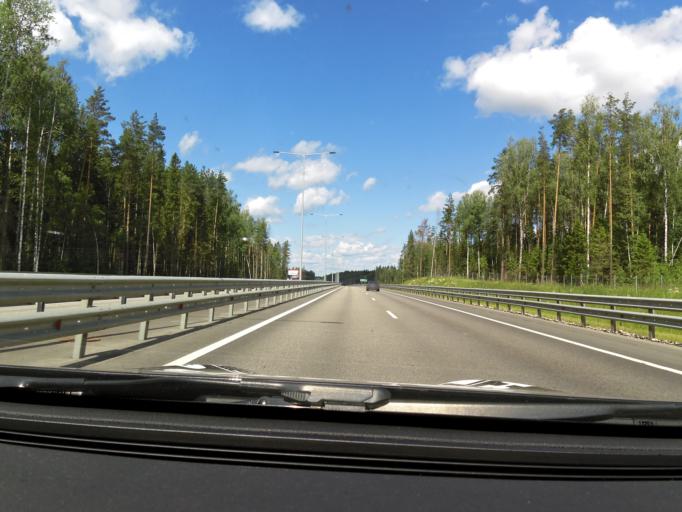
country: RU
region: Tverskaya
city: Vydropuzhsk
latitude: 57.3370
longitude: 34.7305
